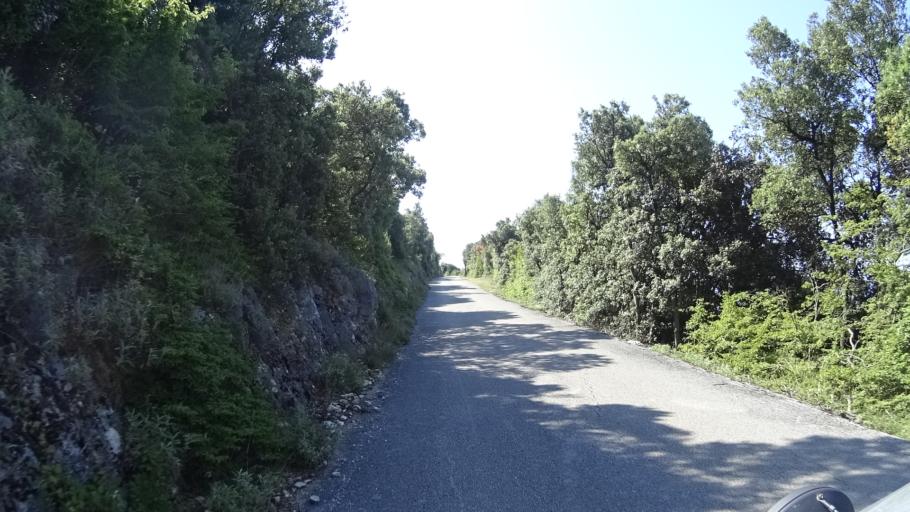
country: HR
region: Istarska
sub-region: Grad Labin
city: Rabac
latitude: 44.9718
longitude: 14.1433
